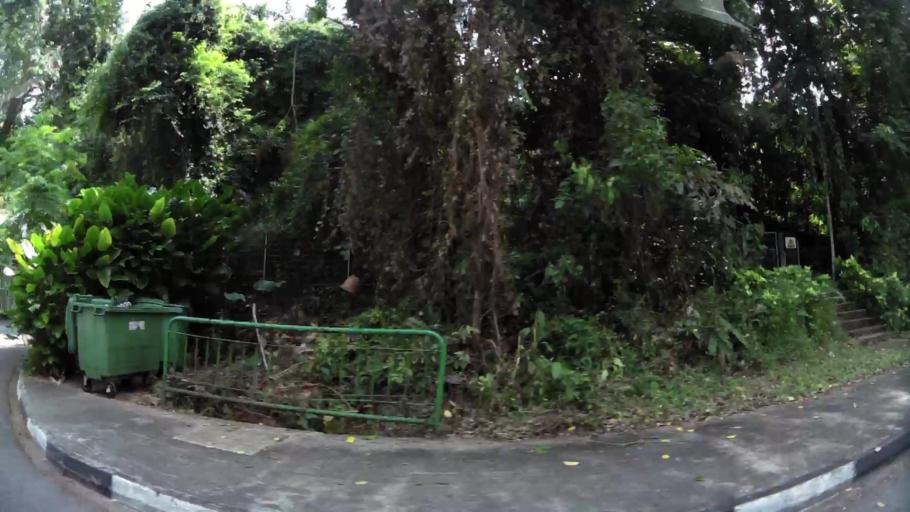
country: MY
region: Johor
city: Kampung Pasir Gudang Baru
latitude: 1.3893
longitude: 103.9788
